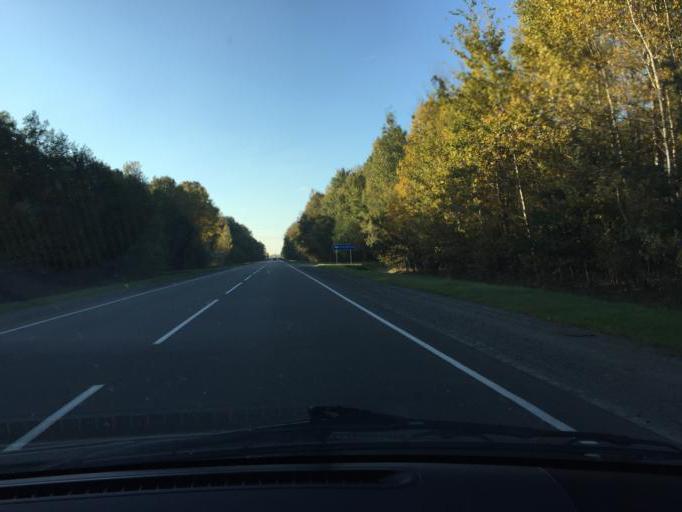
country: BY
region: Brest
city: Horad Luninyets
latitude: 52.3072
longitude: 26.6878
